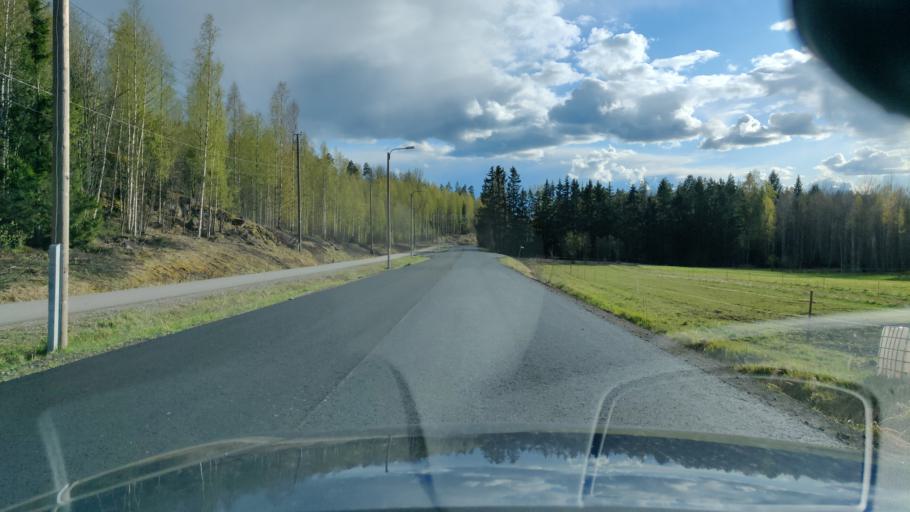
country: FI
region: Uusimaa
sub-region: Helsinki
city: Nurmijaervi
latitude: 60.3737
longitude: 24.7372
